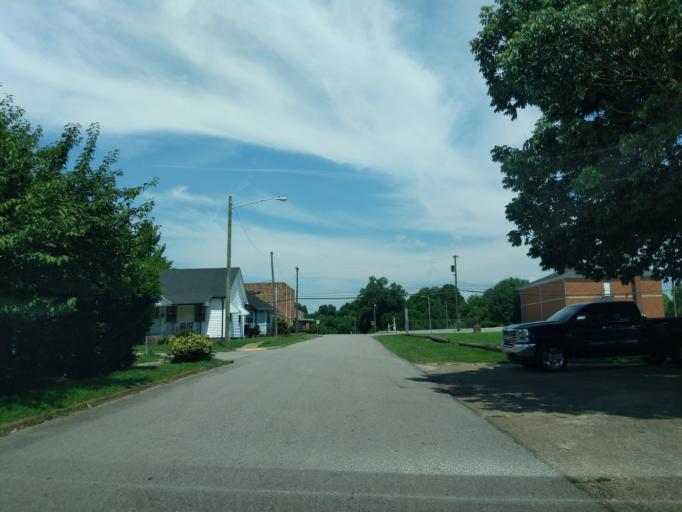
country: US
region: Tennessee
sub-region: Davidson County
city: Lakewood
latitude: 36.2591
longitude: -86.6494
